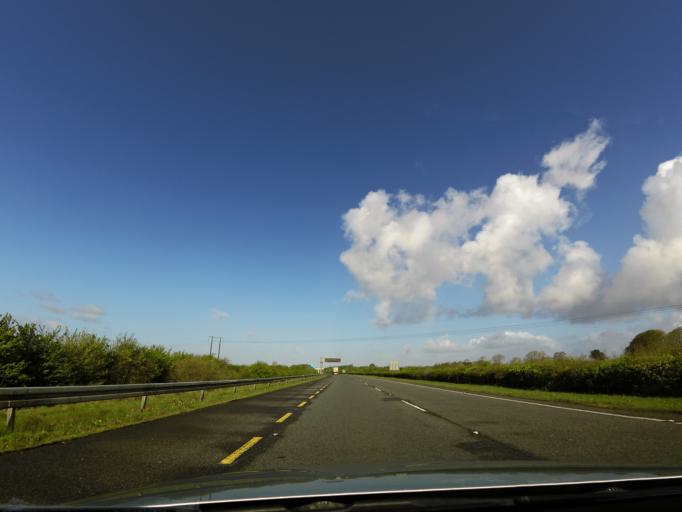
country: IE
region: Munster
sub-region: County Limerick
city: Luimneach
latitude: 52.6393
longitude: -8.6016
